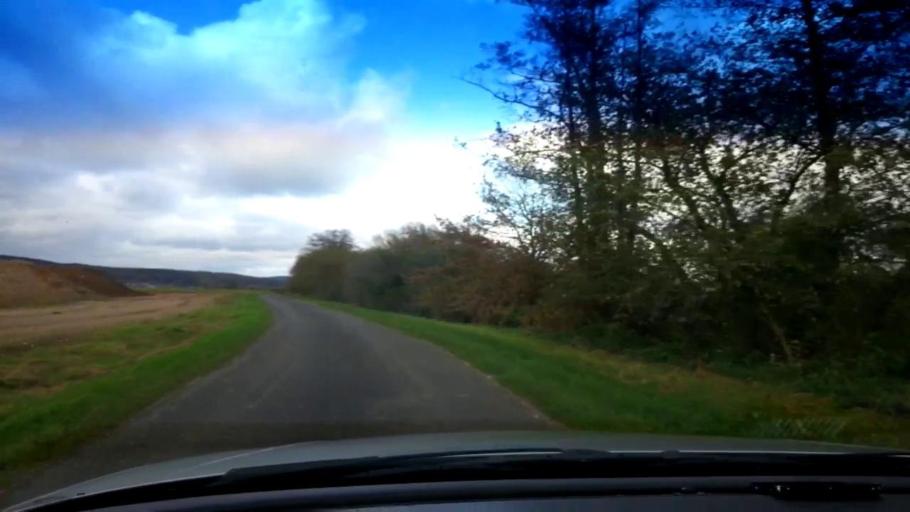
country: DE
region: Bavaria
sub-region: Upper Franconia
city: Zapfendorf
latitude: 50.0288
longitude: 10.9306
